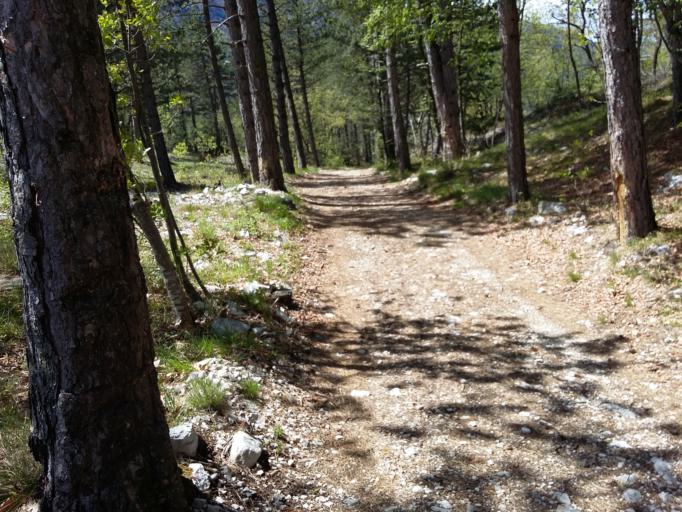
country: IT
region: Trentino-Alto Adige
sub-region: Provincia di Trento
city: Moscheri
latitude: 45.8272
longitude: 11.0894
